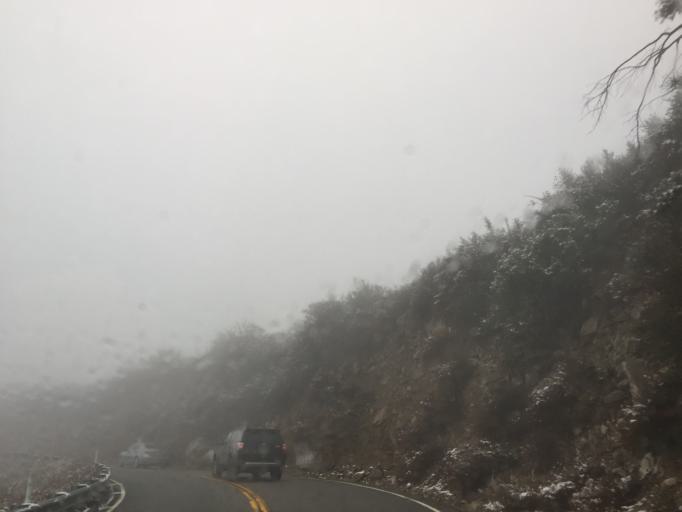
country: US
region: California
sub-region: Los Angeles County
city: Glendora
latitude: 34.3031
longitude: -117.8450
